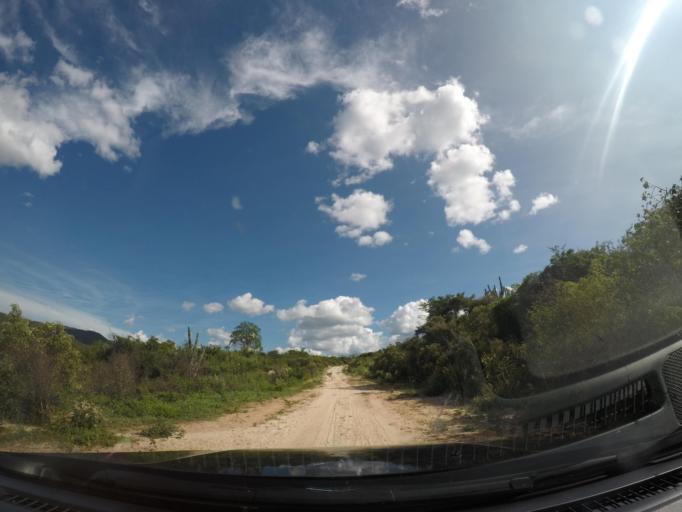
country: BR
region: Bahia
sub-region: Barra Da Estiva
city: Barra da Estiva
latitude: -13.1979
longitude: -41.5952
